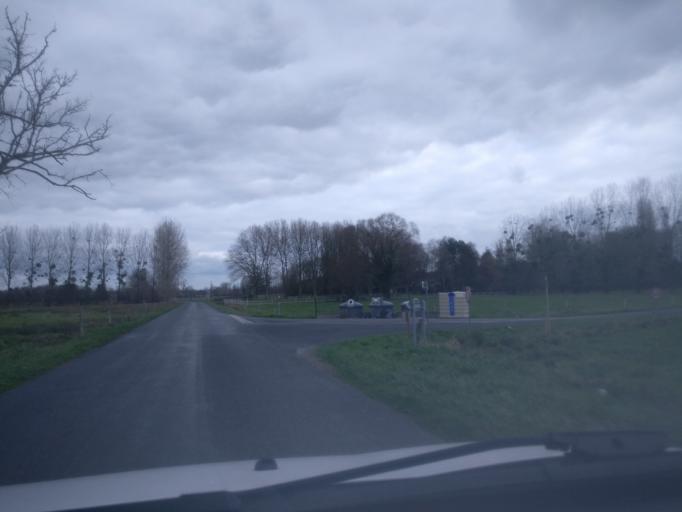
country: FR
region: Lower Normandy
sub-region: Departement de la Manche
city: Marcey-les-Greves
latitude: 48.6763
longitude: -1.4035
